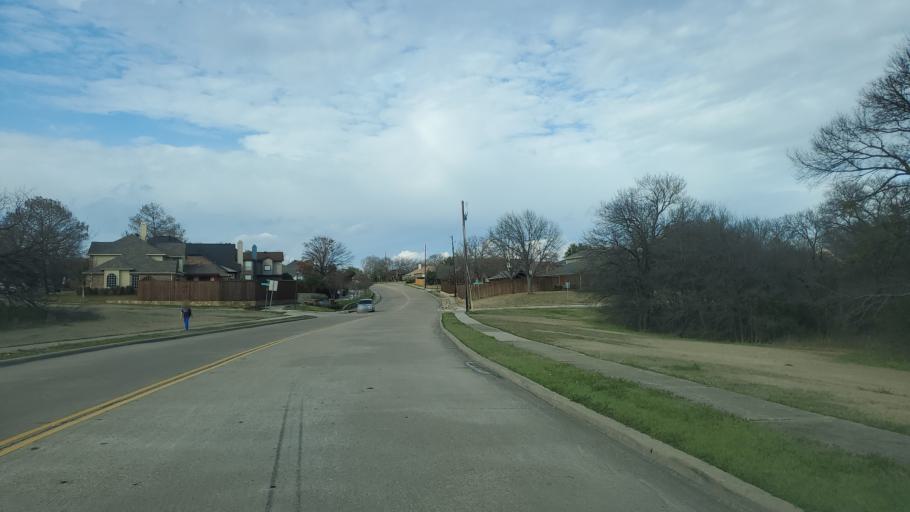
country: US
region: Texas
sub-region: Dallas County
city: Carrollton
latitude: 32.9917
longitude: -96.9019
